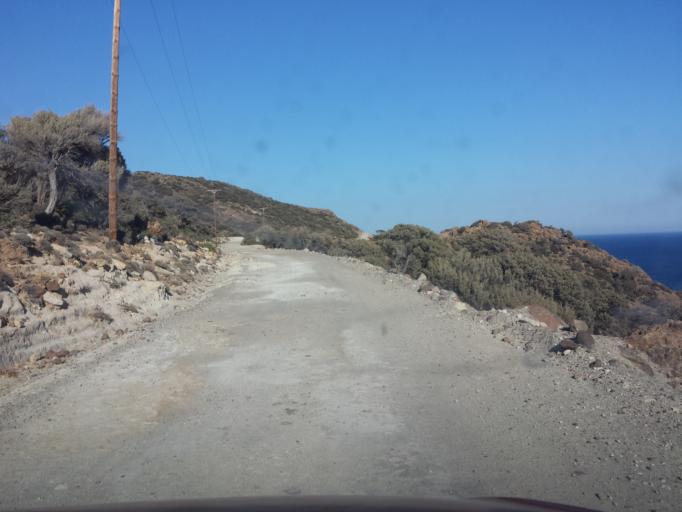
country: GR
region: South Aegean
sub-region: Nomos Kykladon
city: Adamas
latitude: 36.6576
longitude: 24.3752
